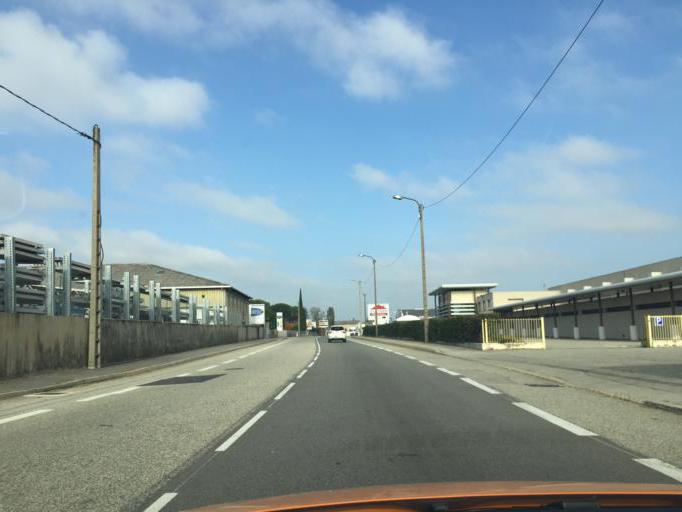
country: FR
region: Rhone-Alpes
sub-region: Departement de la Drome
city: Portes-les-Valence
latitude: 44.8939
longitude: 4.8839
